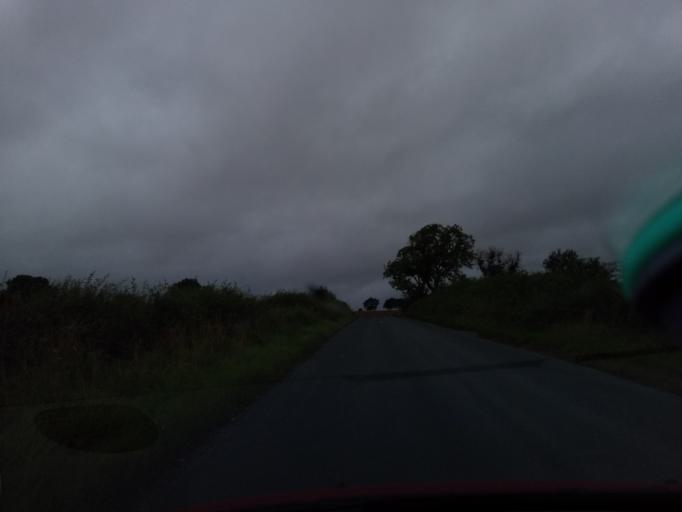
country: GB
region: Scotland
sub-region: The Scottish Borders
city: Kelso
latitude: 55.6144
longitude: -2.4663
